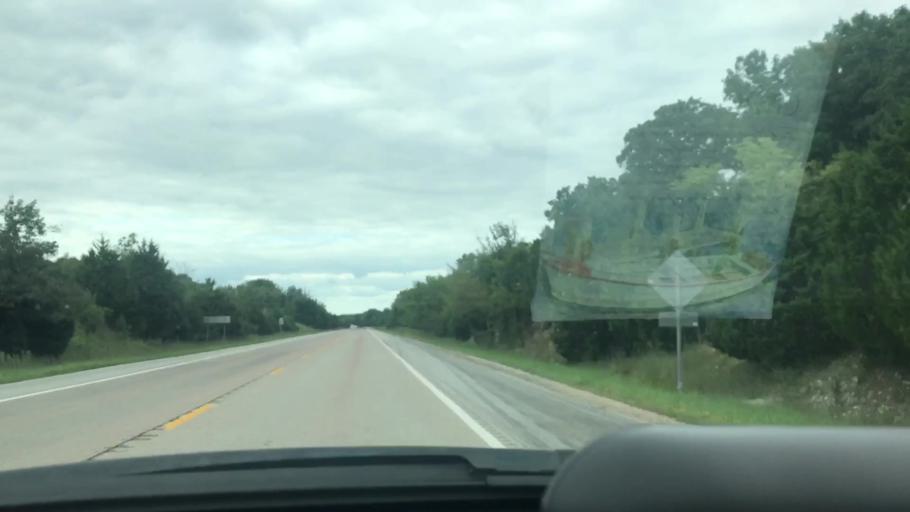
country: US
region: Missouri
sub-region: Benton County
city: Warsaw
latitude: 38.1967
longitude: -93.3250
